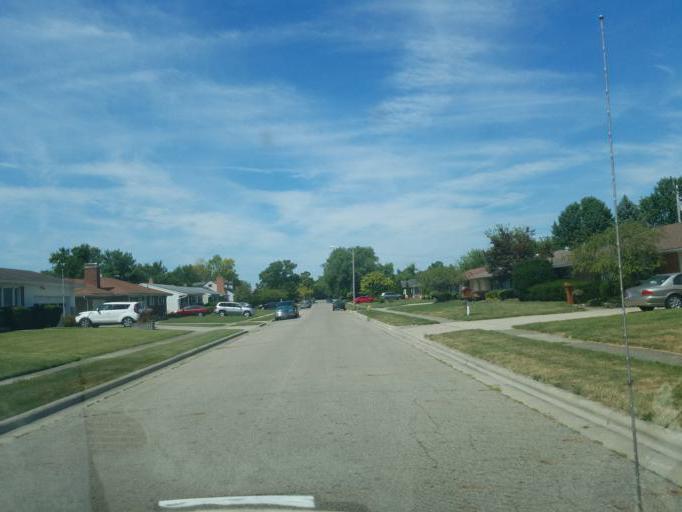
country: US
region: Ohio
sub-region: Franklin County
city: Grove City
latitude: 39.8779
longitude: -83.0724
